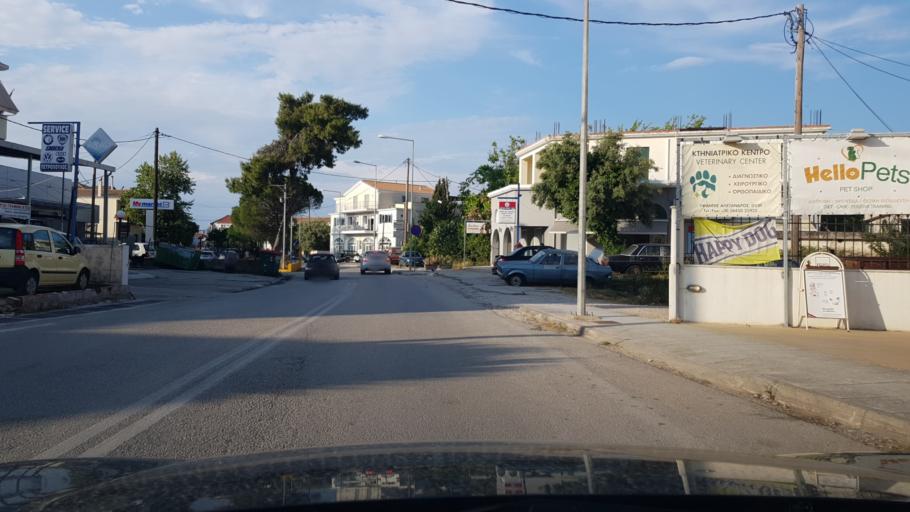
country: GR
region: Ionian Islands
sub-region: Lefkada
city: Lefkada
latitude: 38.8272
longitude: 20.7030
